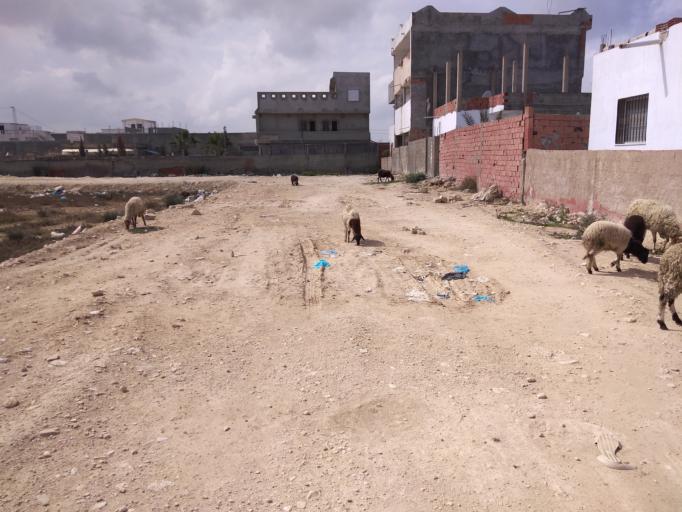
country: TN
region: Ariana
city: Ariana
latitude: 36.9481
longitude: 10.1724
